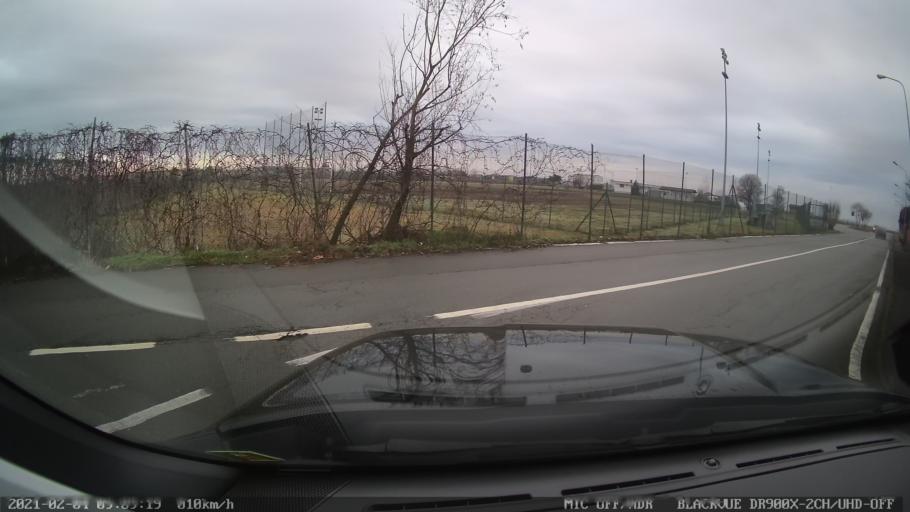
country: IT
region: Piedmont
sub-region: Provincia di Novara
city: San Pietro Mosezzo
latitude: 45.4552
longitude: 8.5484
